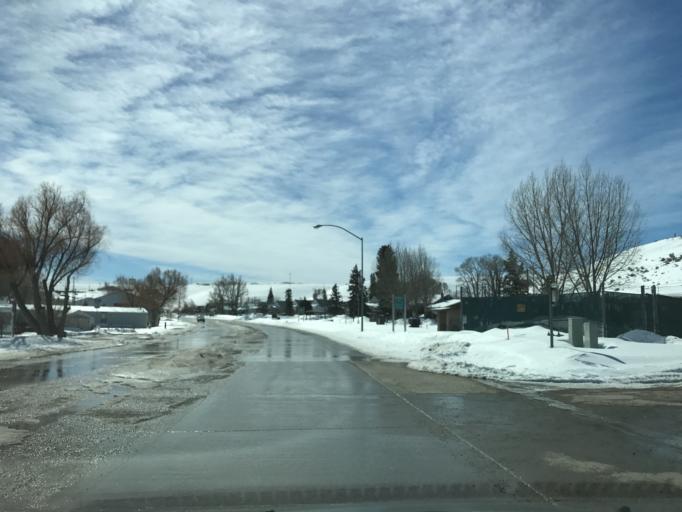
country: US
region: Wyoming
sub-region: Lincoln County
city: Kemmerer
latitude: 41.7808
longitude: -110.5400
